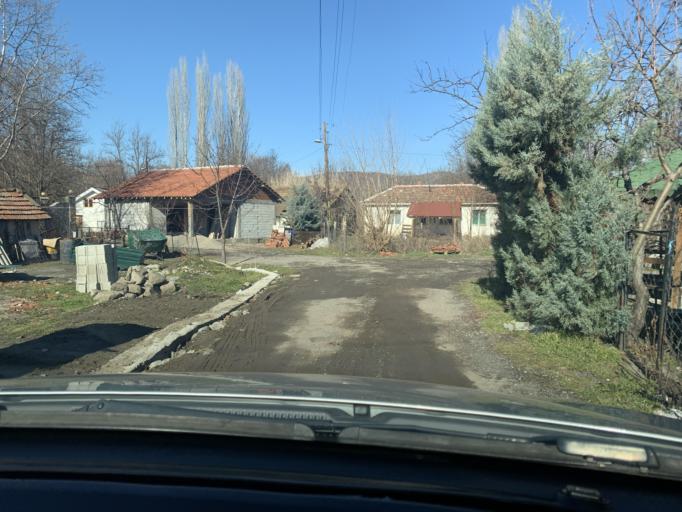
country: MK
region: Demir Kapija
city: Demir Kapija
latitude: 41.3914
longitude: 22.2219
